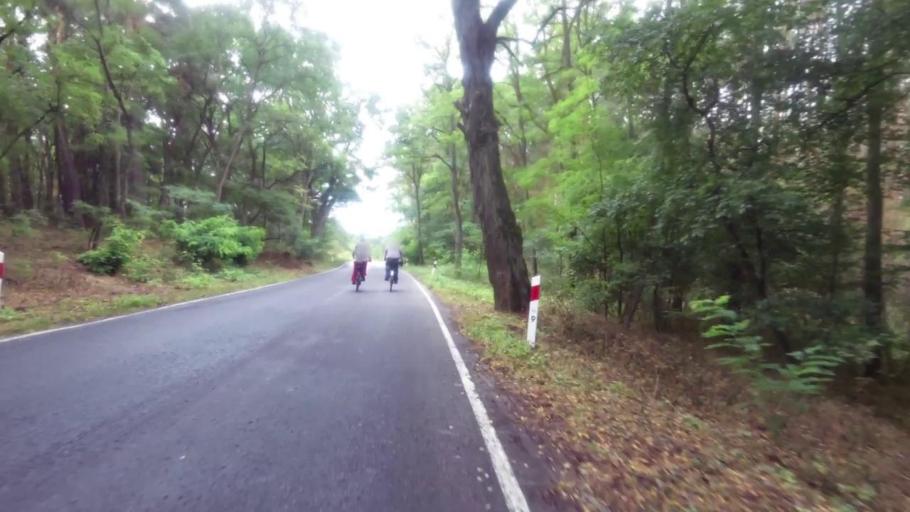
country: PL
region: West Pomeranian Voivodeship
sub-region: Powiat mysliborski
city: Debno
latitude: 52.6921
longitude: 14.6455
